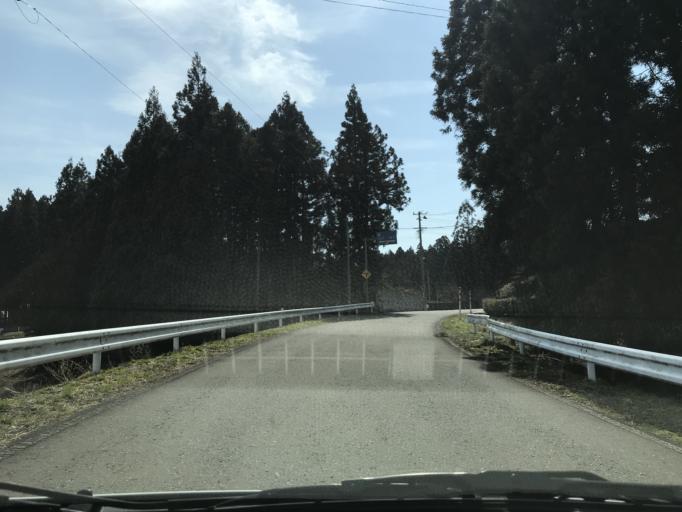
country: JP
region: Iwate
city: Mizusawa
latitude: 39.1184
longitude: 141.0442
